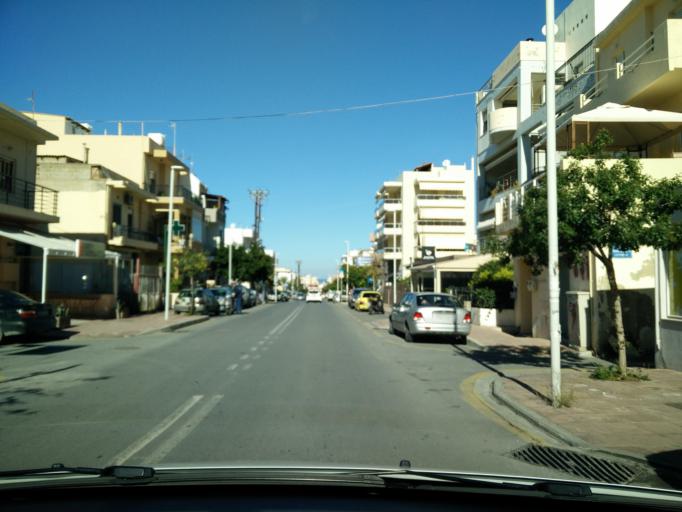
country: GR
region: Crete
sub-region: Nomos Irakleiou
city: Irakleion
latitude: 35.3294
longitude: 25.1447
